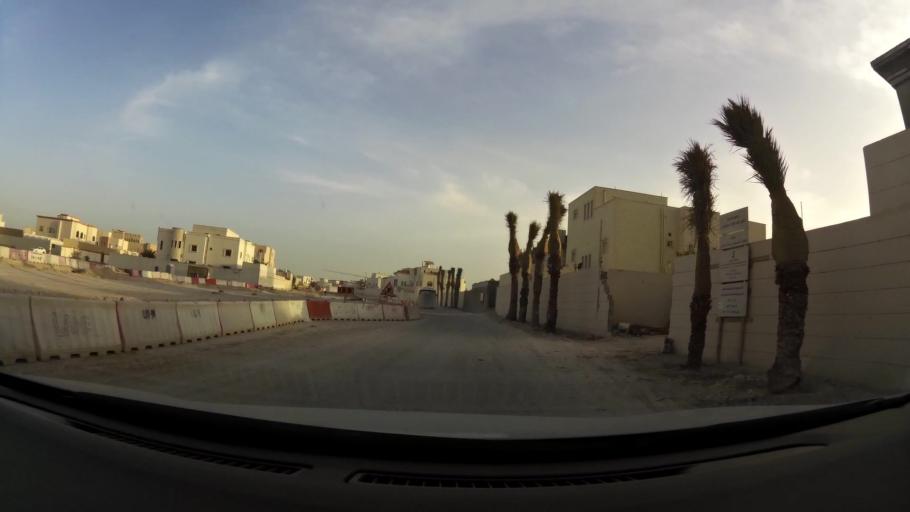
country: QA
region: Al Wakrah
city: Al Wakrah
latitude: 25.1462
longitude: 51.5951
